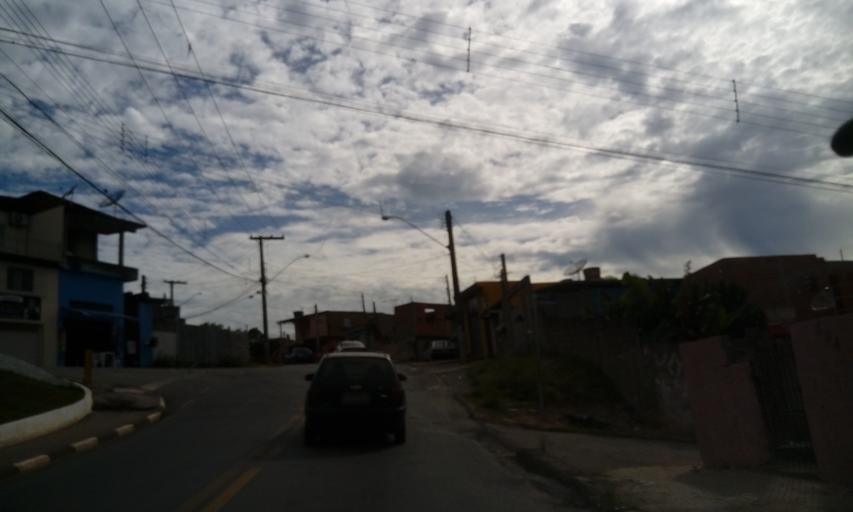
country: BR
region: Sao Paulo
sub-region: Francisco Morato
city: Francisco Morato
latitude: -23.2732
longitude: -46.7413
